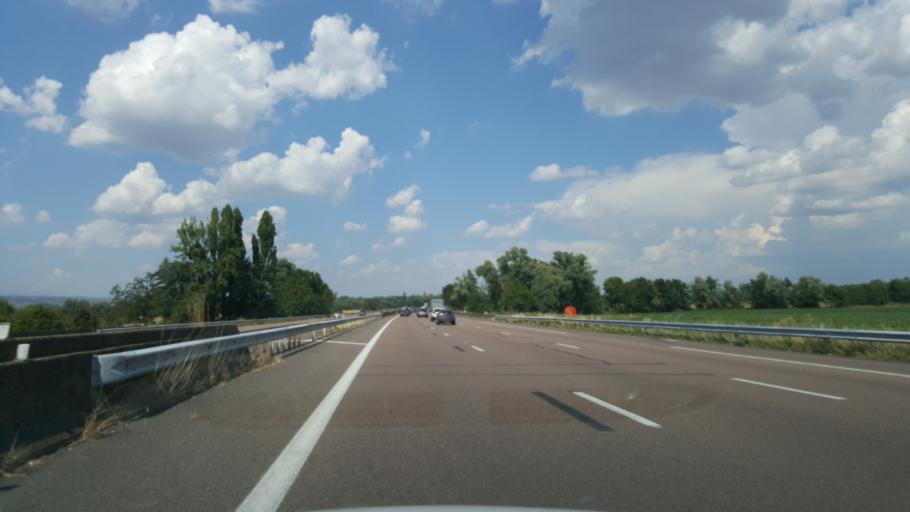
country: FR
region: Bourgogne
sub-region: Departement de Saone-et-Loire
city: Demigny
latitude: 46.9242
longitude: 4.8192
